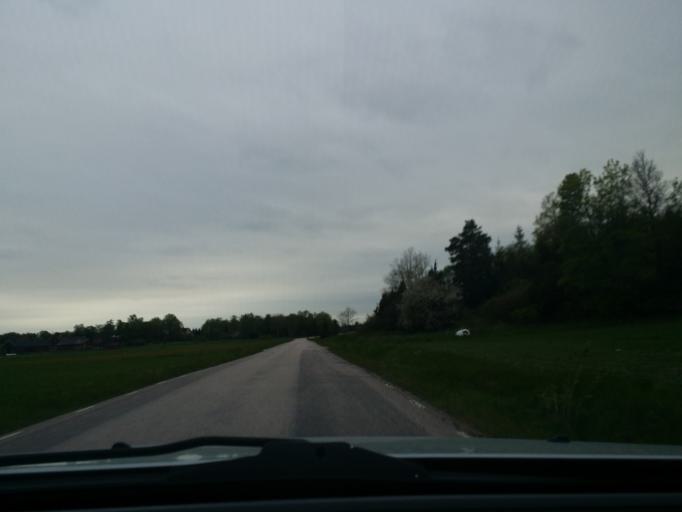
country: SE
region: Vaestmanland
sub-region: Hallstahammars Kommun
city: Kolback
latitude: 59.5471
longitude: 16.3233
